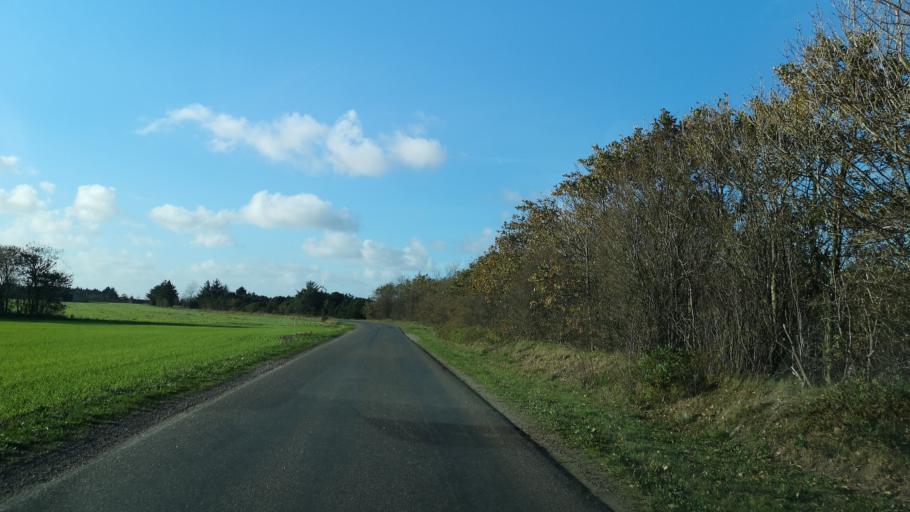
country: DK
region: Central Jutland
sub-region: Ringkobing-Skjern Kommune
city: Skjern
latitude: 55.8355
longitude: 8.3666
